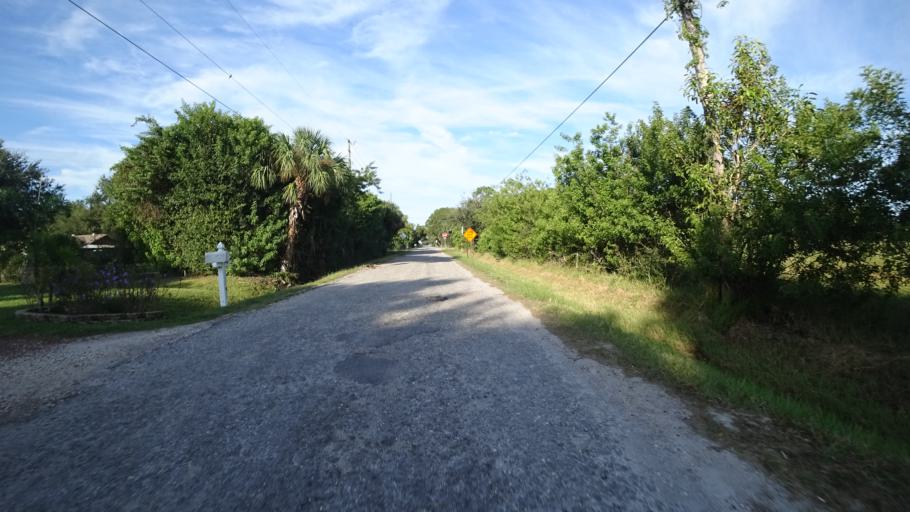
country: US
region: Florida
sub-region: Manatee County
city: Samoset
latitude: 27.4656
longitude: -82.5127
